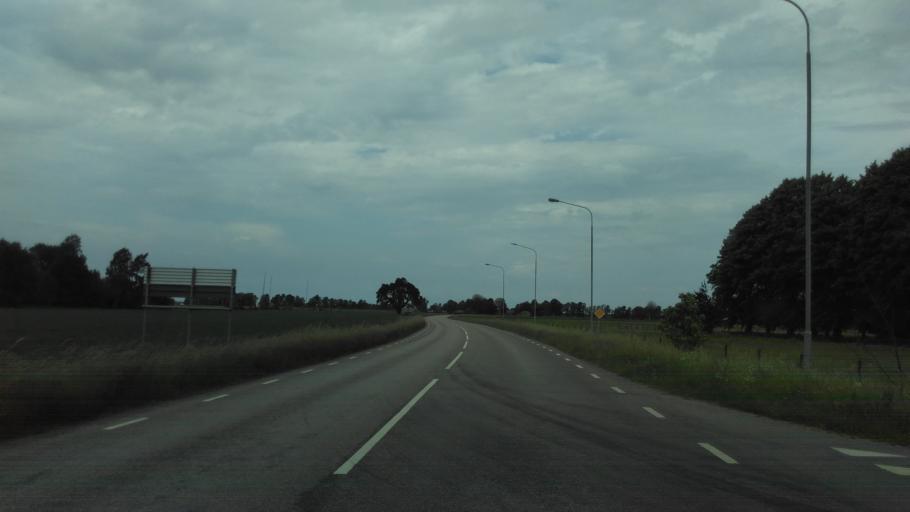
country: SE
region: Vaestra Goetaland
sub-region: Lidkopings Kommun
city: Lidkoping
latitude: 58.4400
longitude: 13.1623
